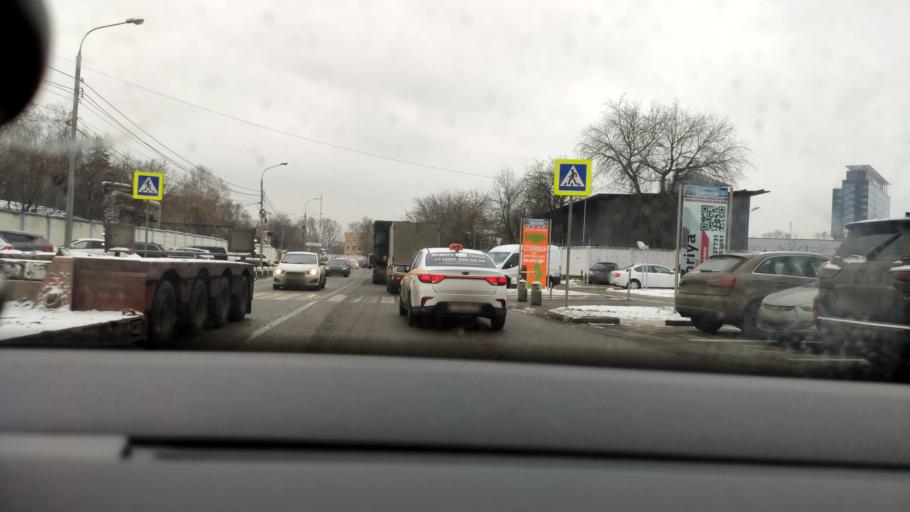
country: RU
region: Moscow
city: Khimki
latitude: 55.9116
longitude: 37.4197
